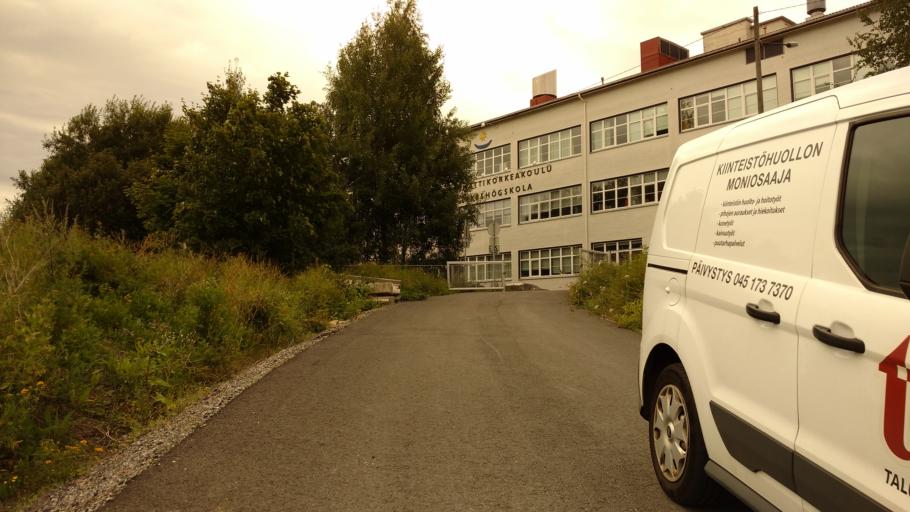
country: FI
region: Varsinais-Suomi
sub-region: Turku
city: Turku
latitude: 60.4484
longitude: 22.2996
